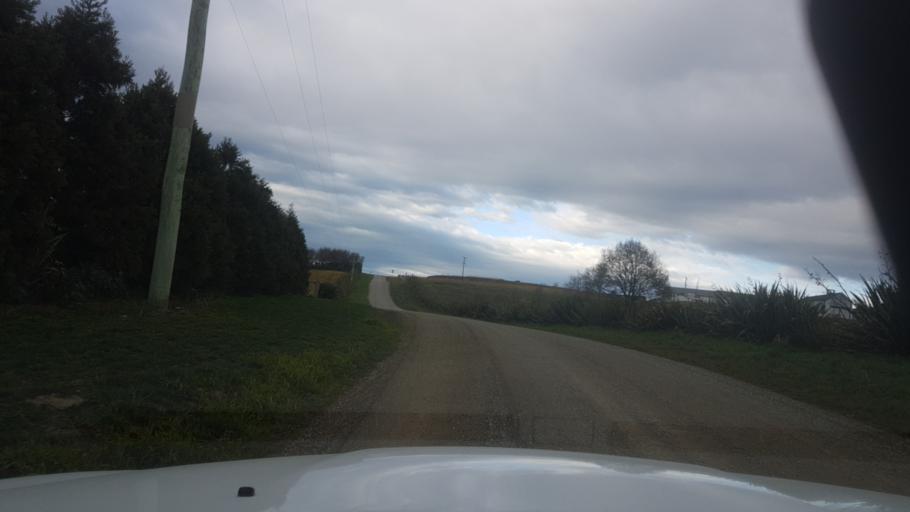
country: NZ
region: Canterbury
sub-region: Timaru District
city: Pleasant Point
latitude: -44.3517
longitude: 171.1556
